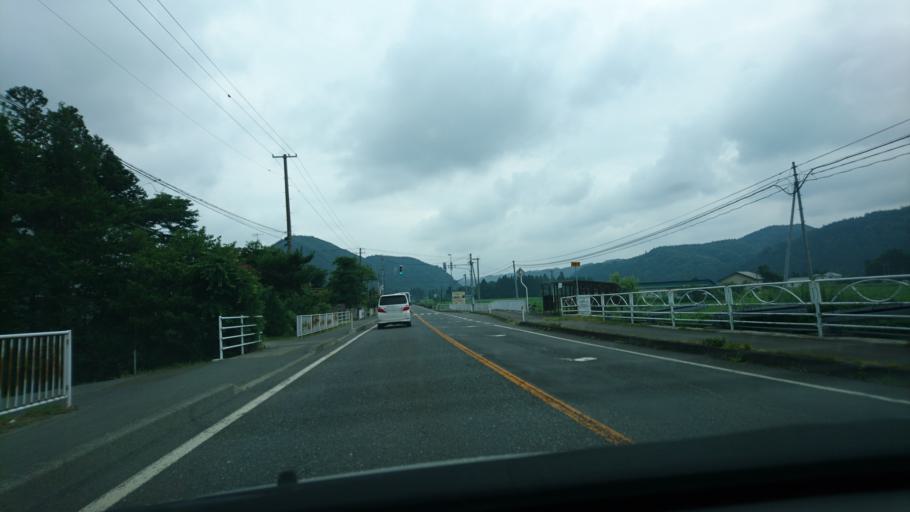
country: JP
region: Miyagi
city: Furukawa
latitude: 38.7311
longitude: 140.7920
